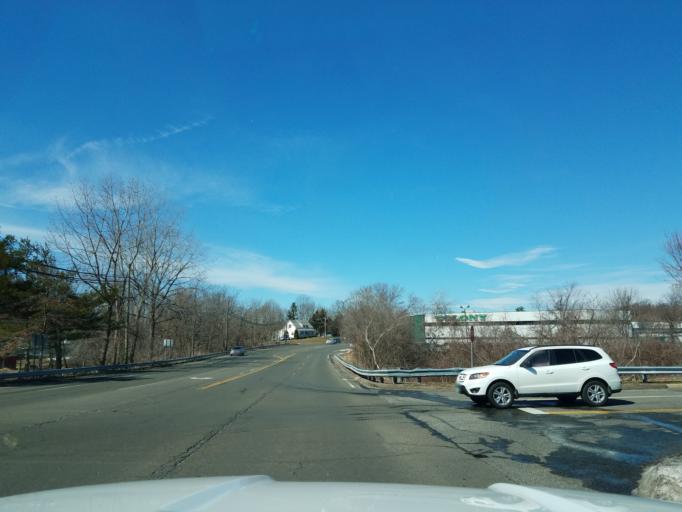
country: US
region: Connecticut
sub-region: New Haven County
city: Orange
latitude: 41.2601
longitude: -73.0032
